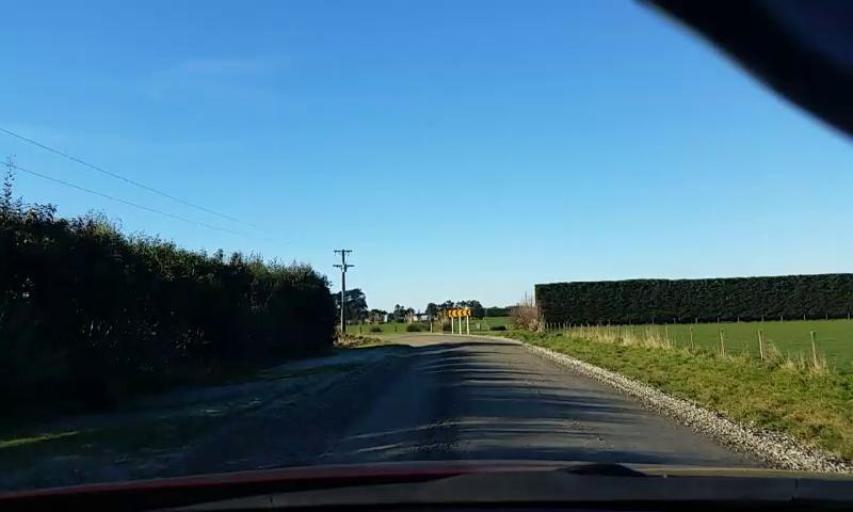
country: NZ
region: Southland
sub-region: Invercargill City
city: Invercargill
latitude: -46.3572
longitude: 168.4306
